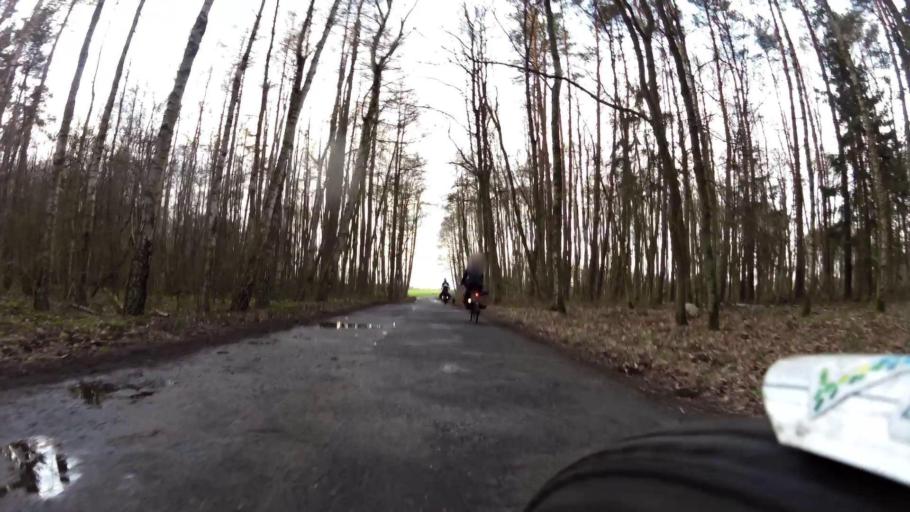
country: PL
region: West Pomeranian Voivodeship
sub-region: Powiat kamienski
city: Kamien Pomorski
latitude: 53.9094
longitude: 14.7318
